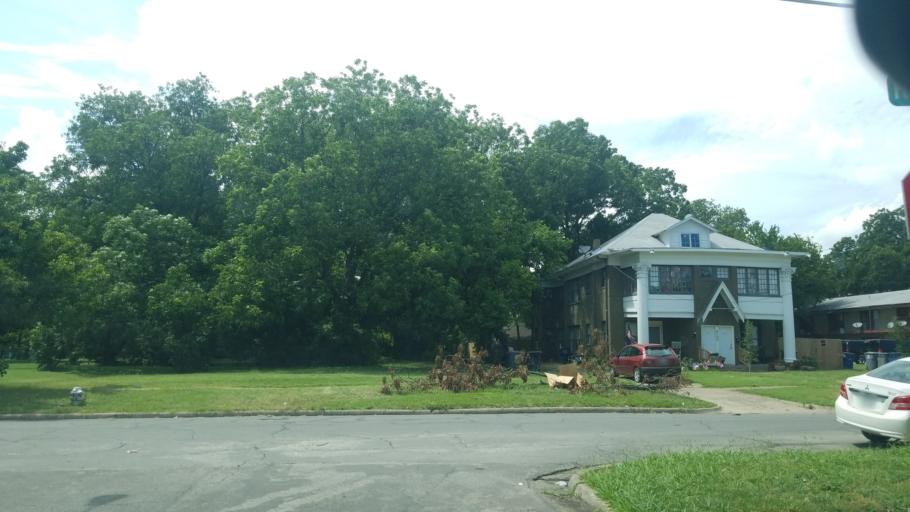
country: US
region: Texas
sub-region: Dallas County
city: Dallas
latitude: 32.7944
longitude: -96.7668
